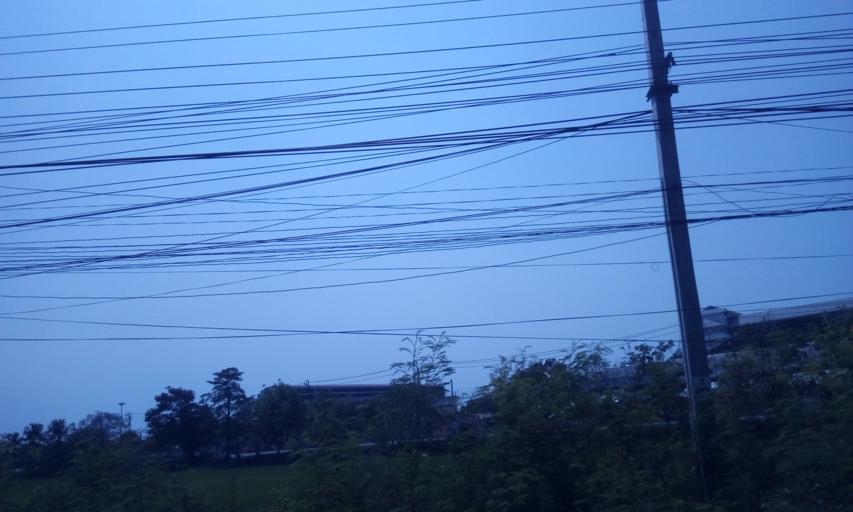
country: TH
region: Nonthaburi
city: Sai Noi
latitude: 13.9754
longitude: 100.3101
